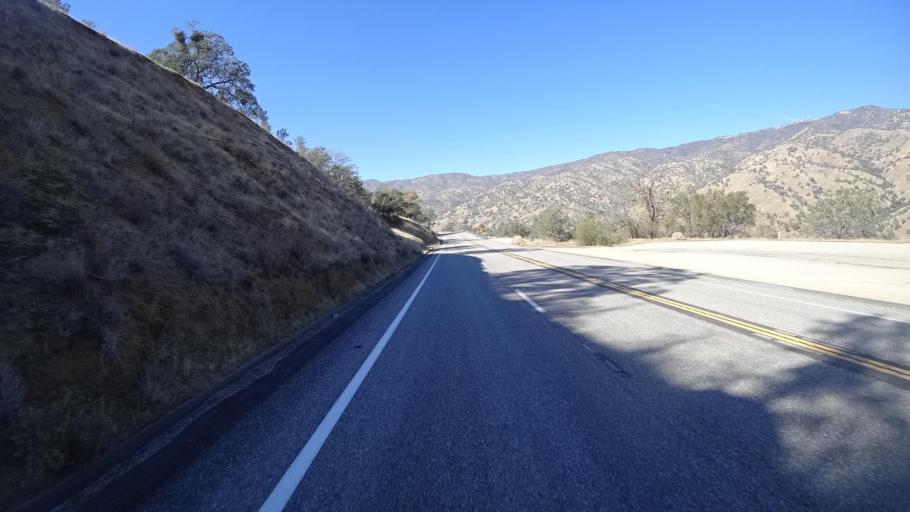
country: US
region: California
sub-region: Kern County
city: Bodfish
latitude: 35.5308
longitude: -118.6440
